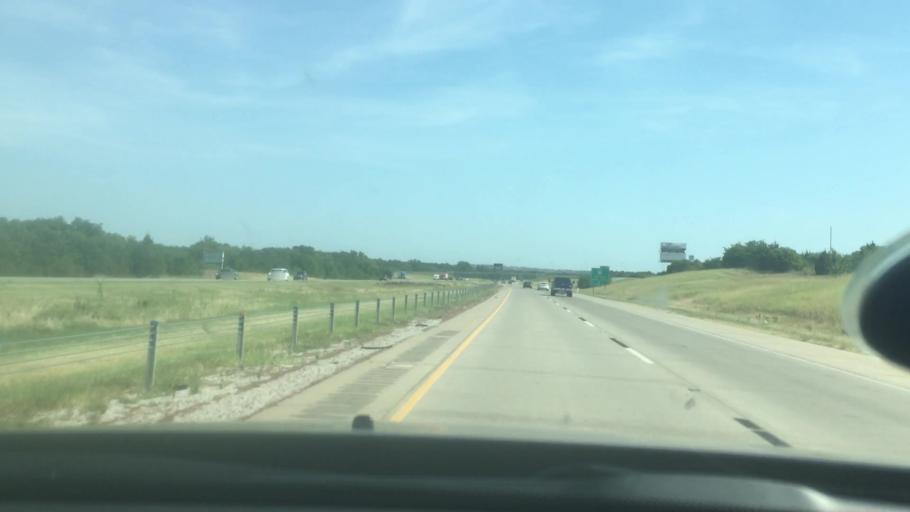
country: US
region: Oklahoma
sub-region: Carter County
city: Ardmore
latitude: 34.2966
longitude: -97.1591
